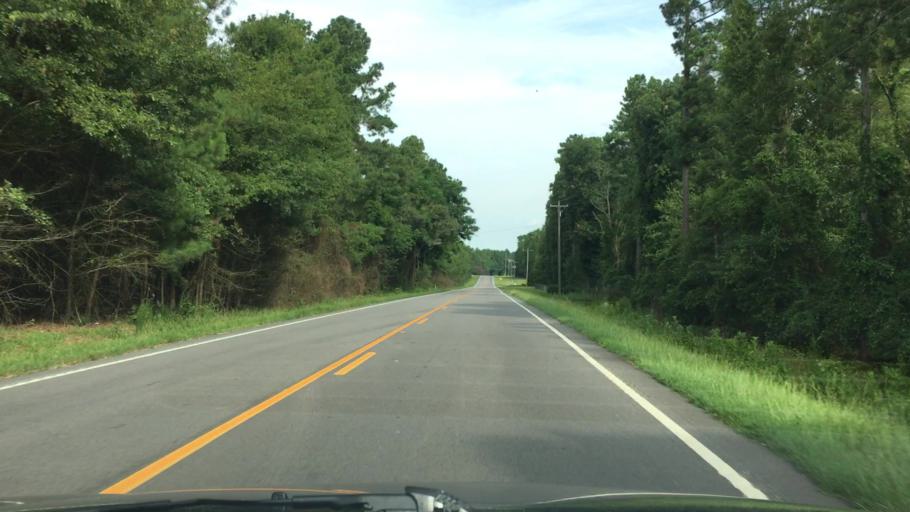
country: US
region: South Carolina
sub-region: Lexington County
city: Batesburg-Leesville
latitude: 33.7077
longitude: -81.4898
